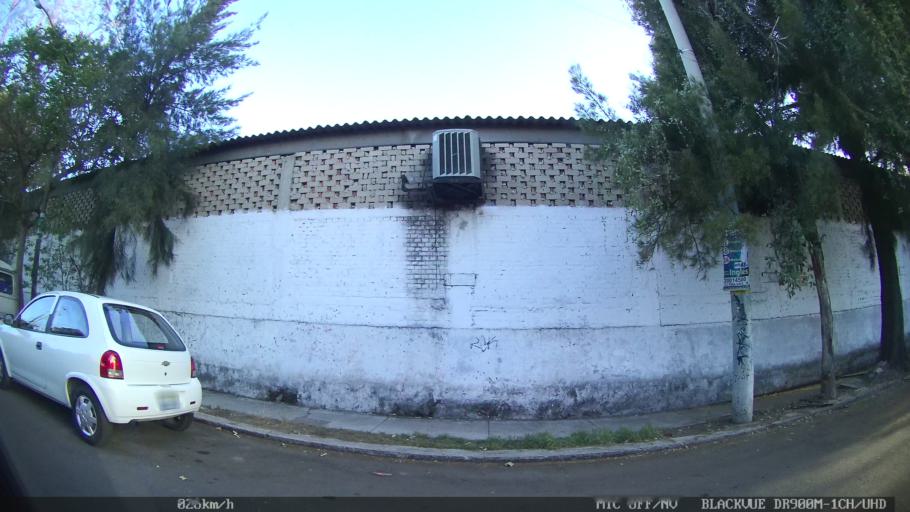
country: MX
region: Jalisco
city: Tlaquepaque
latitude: 20.7094
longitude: -103.3047
